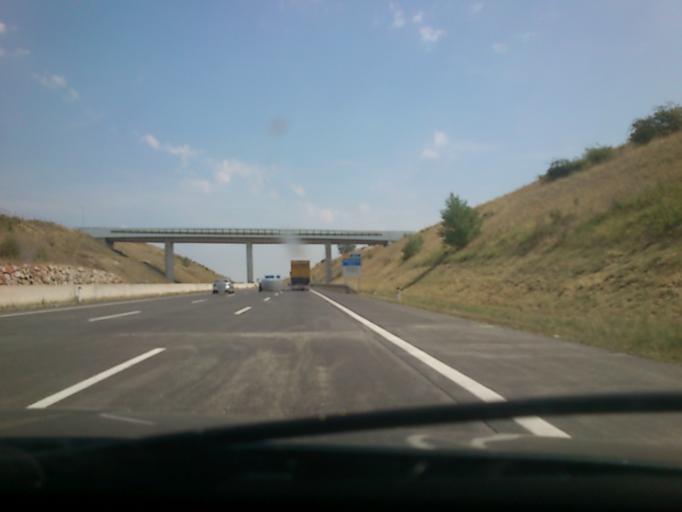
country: AT
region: Lower Austria
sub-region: Politischer Bezirk Mistelbach
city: Wolkersdorf im Weinviertel
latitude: 48.3987
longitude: 16.5195
